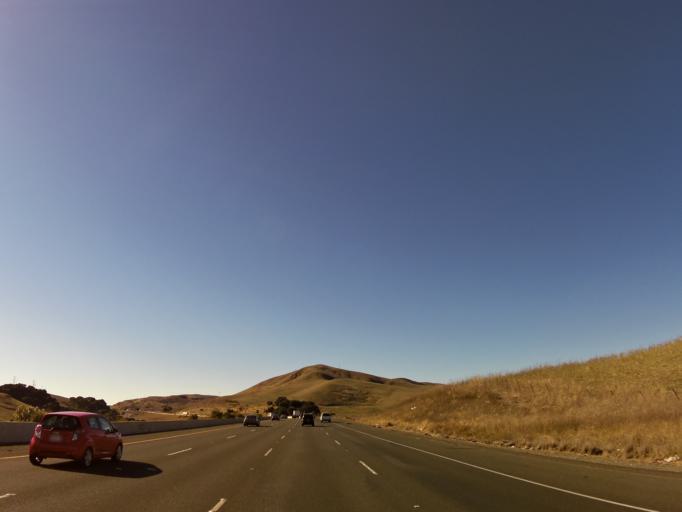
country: US
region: California
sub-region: Solano County
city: Green Valley
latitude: 38.1870
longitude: -122.1765
